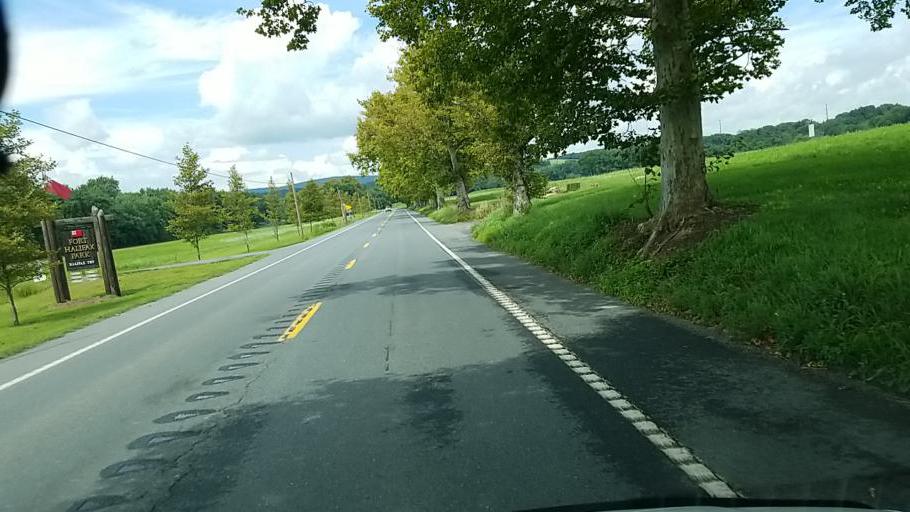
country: US
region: Pennsylvania
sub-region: Dauphin County
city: Matamoras
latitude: 40.4776
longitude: -76.9313
